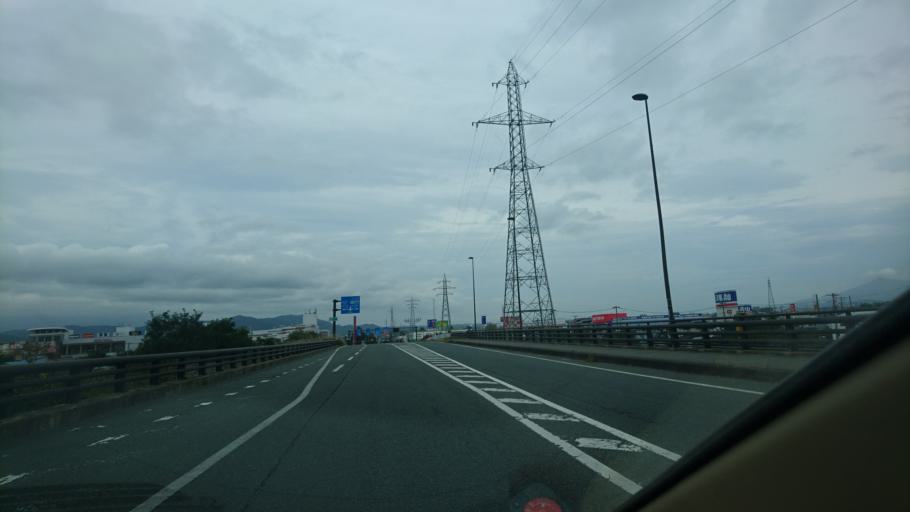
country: JP
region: Iwate
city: Morioka-shi
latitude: 39.7075
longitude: 141.1016
